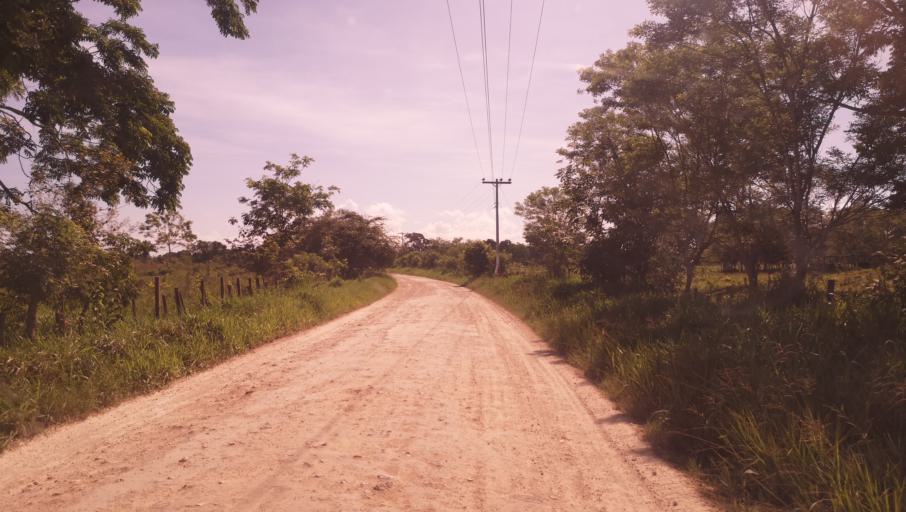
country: GT
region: Peten
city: Dolores
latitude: 16.7148
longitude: -89.3654
